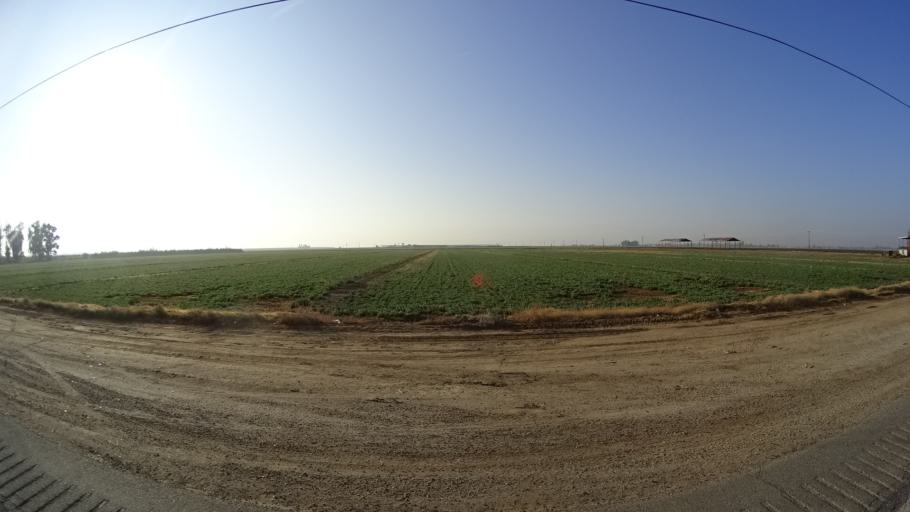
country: US
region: California
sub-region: Kern County
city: Lamont
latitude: 35.2670
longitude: -118.9476
